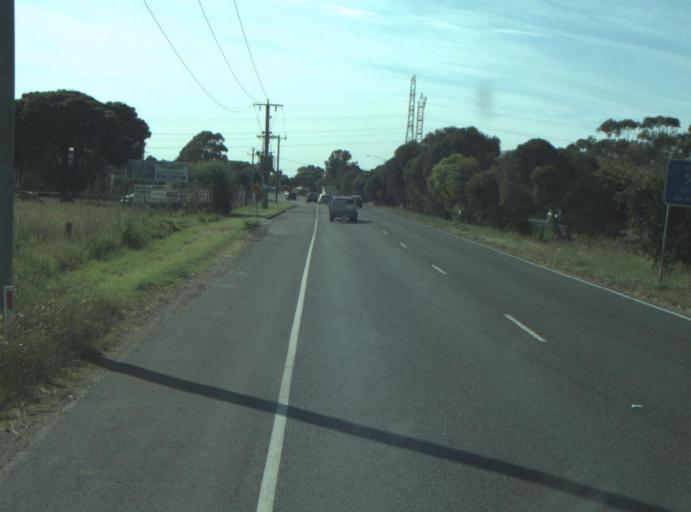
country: AU
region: Victoria
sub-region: Greater Geelong
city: Leopold
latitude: -38.1692
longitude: 144.4257
